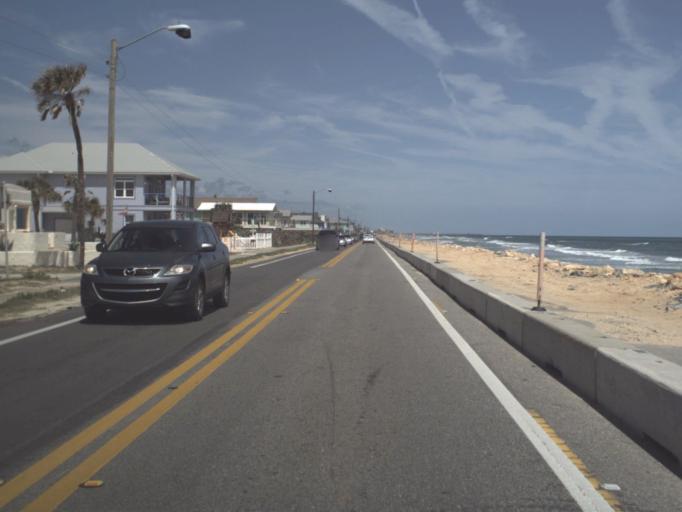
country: US
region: Florida
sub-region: Flagler County
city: Flagler Beach
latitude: 29.4637
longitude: -81.1191
